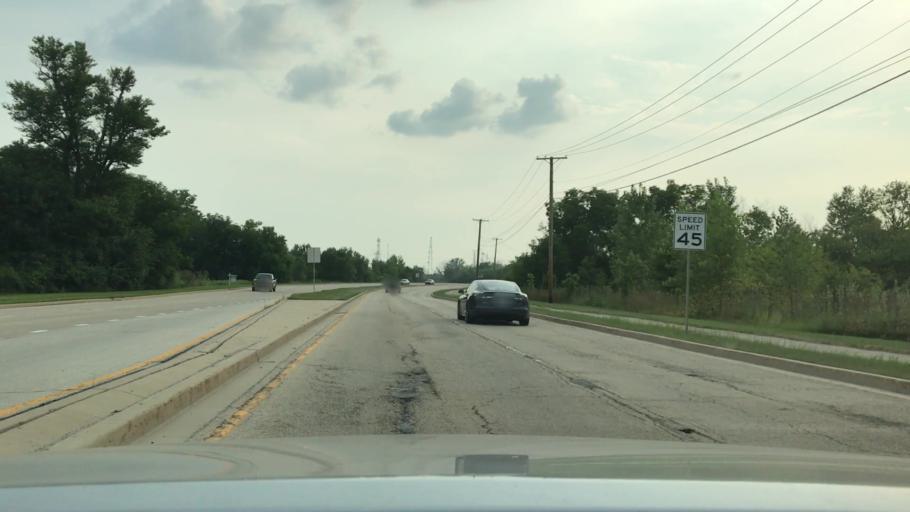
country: US
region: Illinois
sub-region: DuPage County
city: Warrenville
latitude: 41.8097
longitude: -88.2177
